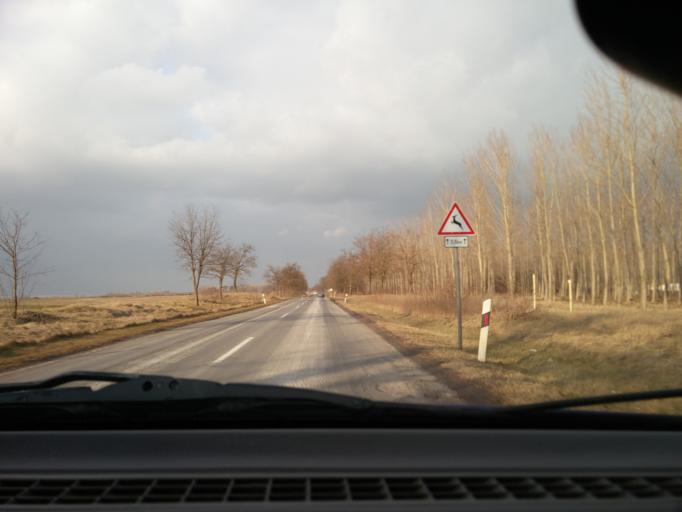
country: HU
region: Pest
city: Tapioszolos
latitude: 47.3042
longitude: 19.8708
